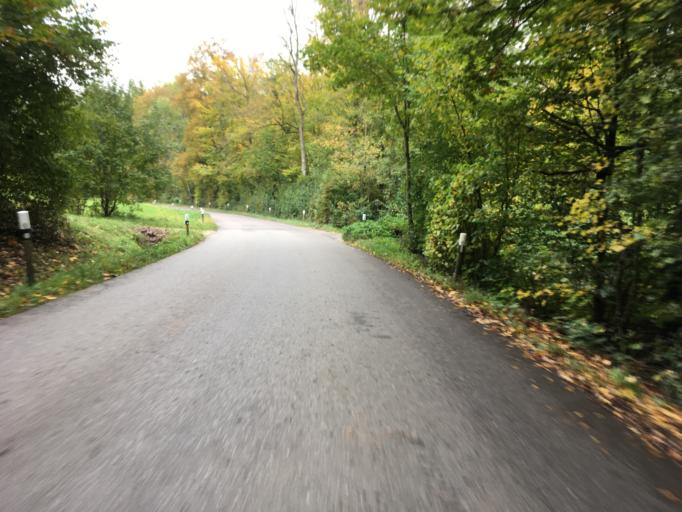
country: DE
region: Baden-Wuerttemberg
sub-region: Tuebingen Region
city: Dusslingen
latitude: 48.4831
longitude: 9.0625
